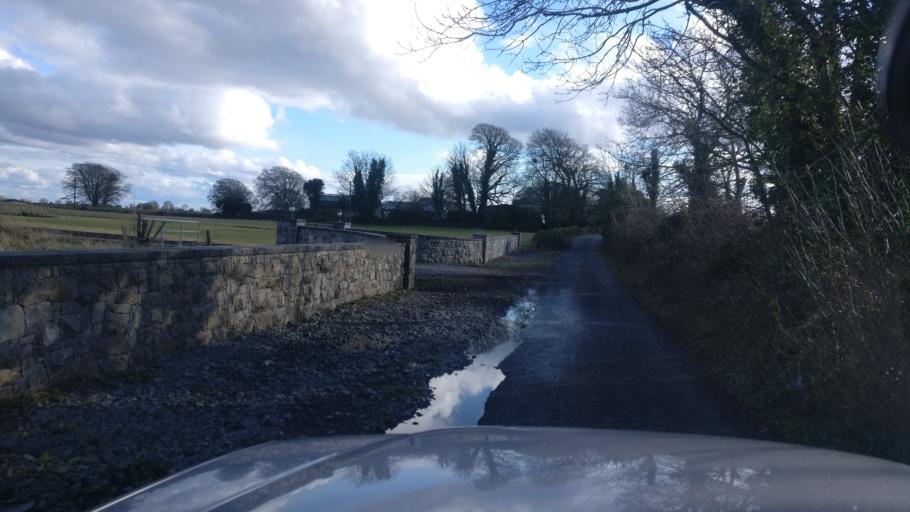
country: IE
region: Connaught
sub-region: County Galway
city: Loughrea
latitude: 53.1783
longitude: -8.4260
